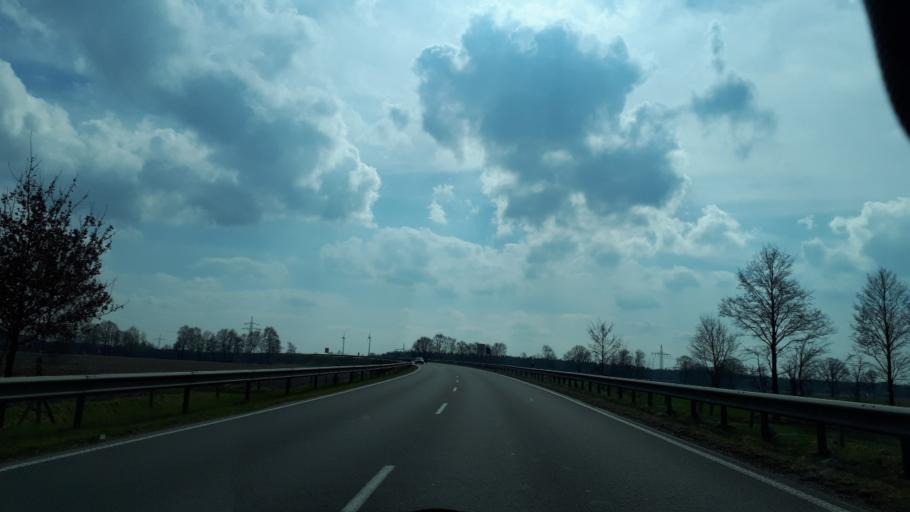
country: DE
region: Lower Saxony
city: Vechta
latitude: 52.7365
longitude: 8.2498
